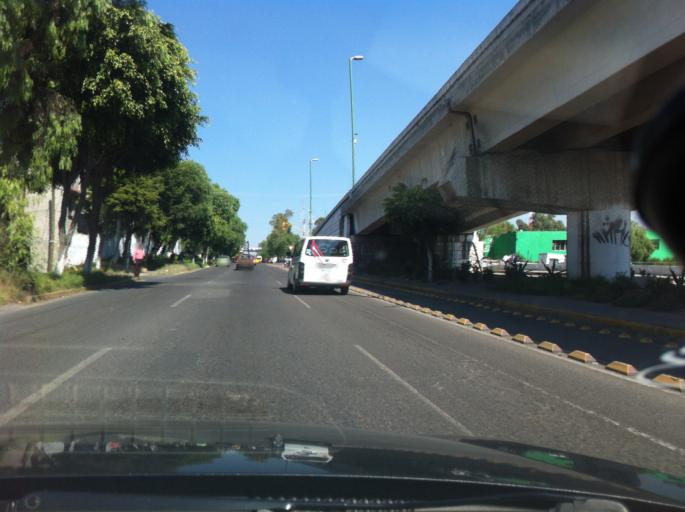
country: MX
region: Mexico
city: Cuautitlan Izcalli
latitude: 19.6494
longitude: -99.2087
